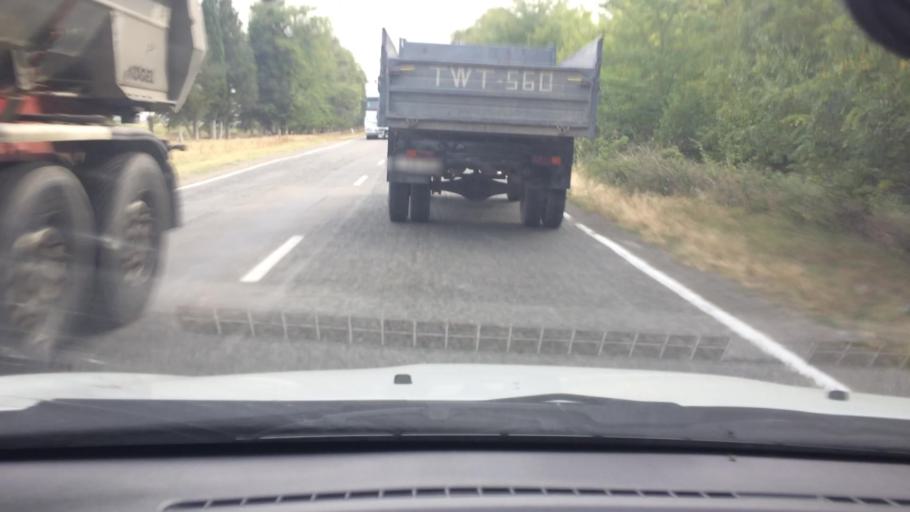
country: GE
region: Kvemo Kartli
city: Rust'avi
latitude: 41.4642
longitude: 44.9839
